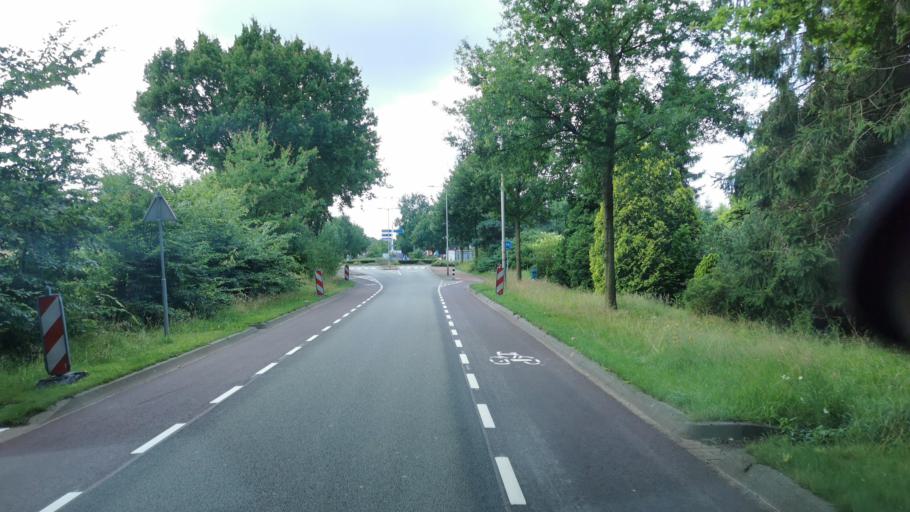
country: NL
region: Overijssel
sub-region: Gemeente Losser
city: Losser
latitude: 52.2678
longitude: 6.9936
